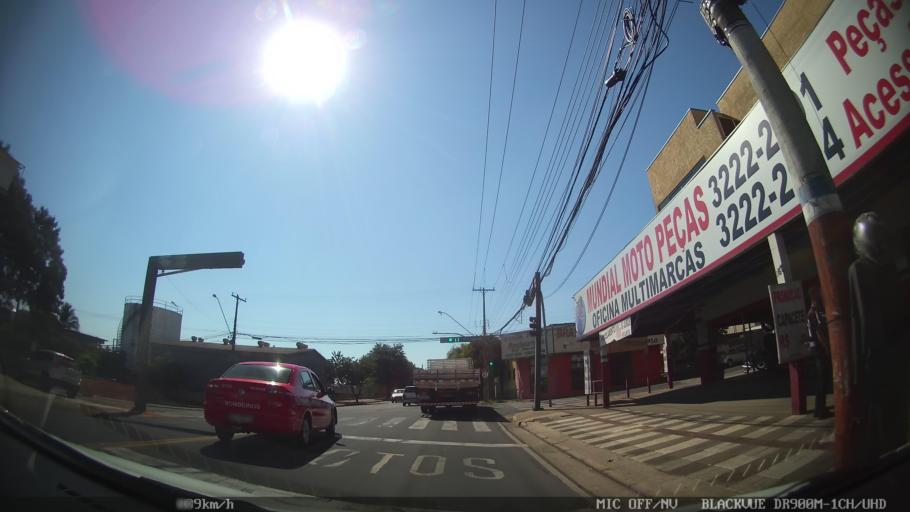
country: BR
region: Sao Paulo
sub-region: Sao Jose Do Rio Preto
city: Sao Jose do Rio Preto
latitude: -20.7952
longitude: -49.3907
